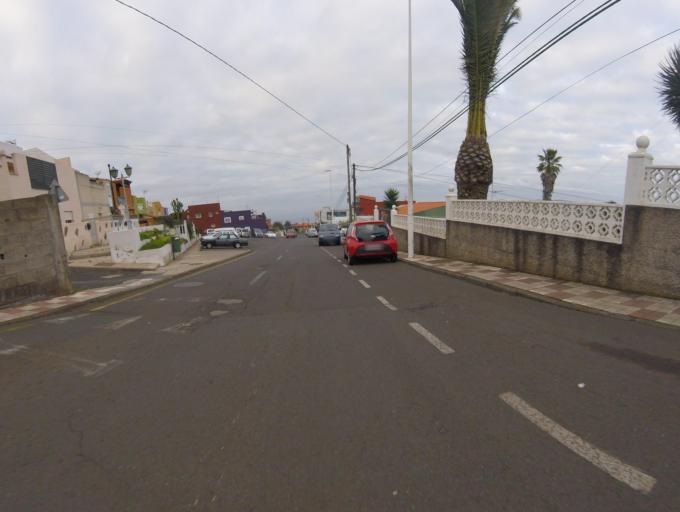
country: ES
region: Canary Islands
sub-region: Provincia de Santa Cruz de Tenerife
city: La Laguna
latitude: 28.4572
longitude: -16.3623
